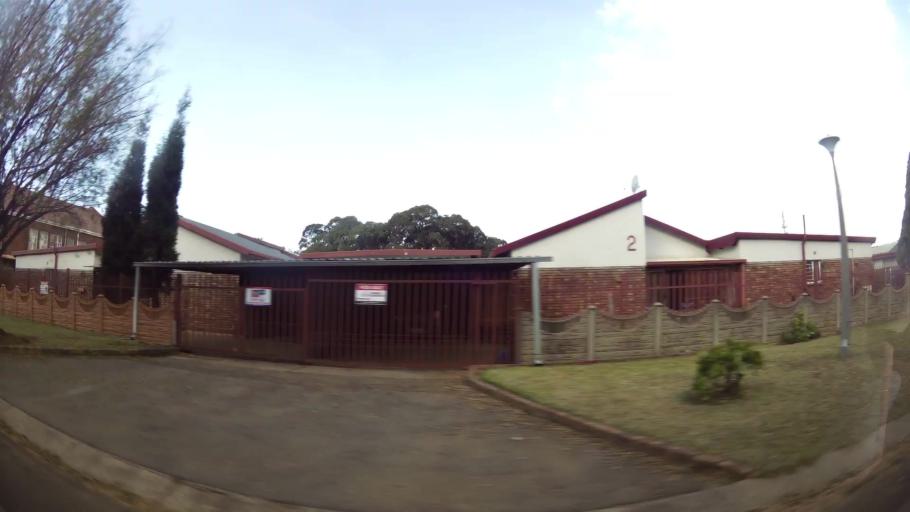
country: ZA
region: Mpumalanga
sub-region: Nkangala District Municipality
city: Witbank
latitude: -25.9210
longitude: 29.2199
